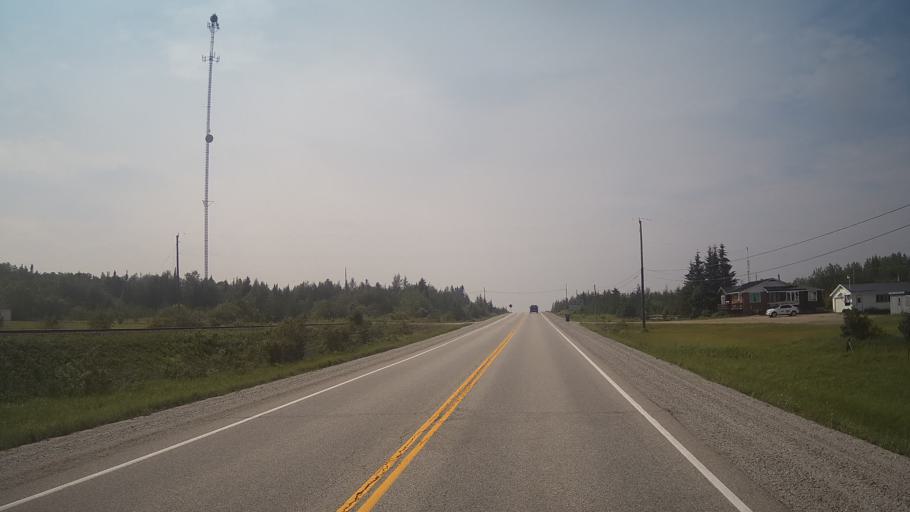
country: CA
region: Ontario
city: Kapuskasing
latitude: 49.3219
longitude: -82.0629
